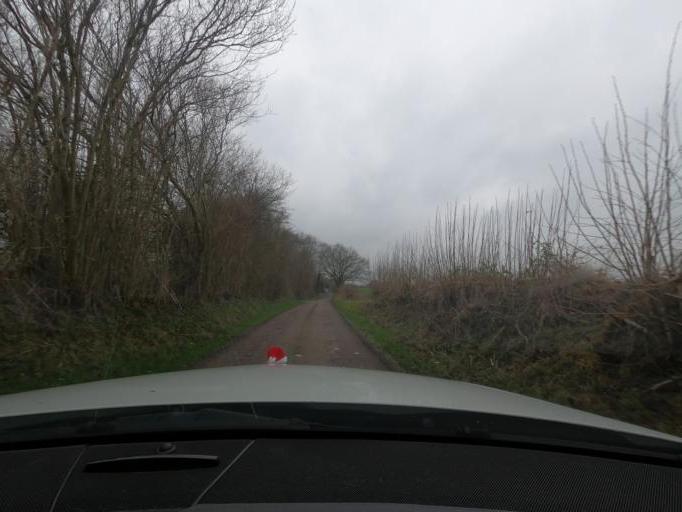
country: DK
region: South Denmark
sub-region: Haderslev Kommune
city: Starup
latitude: 55.2402
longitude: 9.7107
